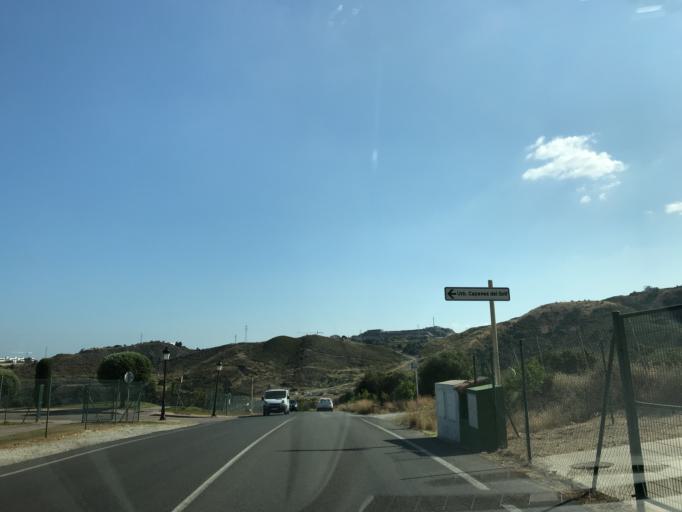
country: ES
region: Andalusia
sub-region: Provincia de Malaga
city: Benahavis
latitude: 36.5054
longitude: -5.0237
